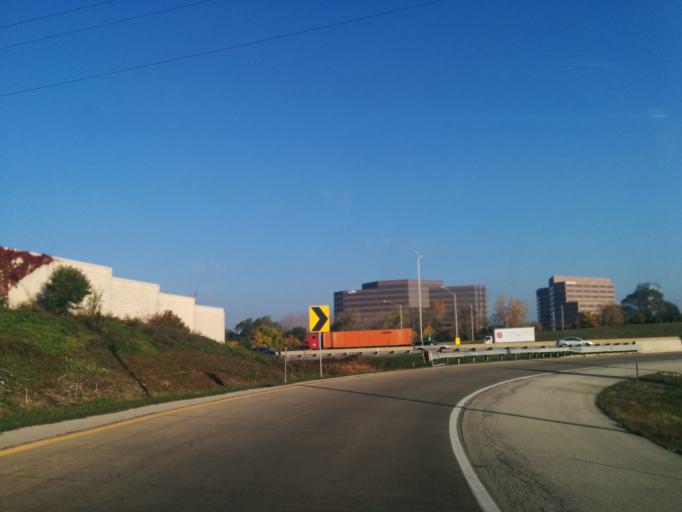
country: US
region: Illinois
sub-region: DuPage County
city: Oakbrook Terrace
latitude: 41.8437
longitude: -87.9592
